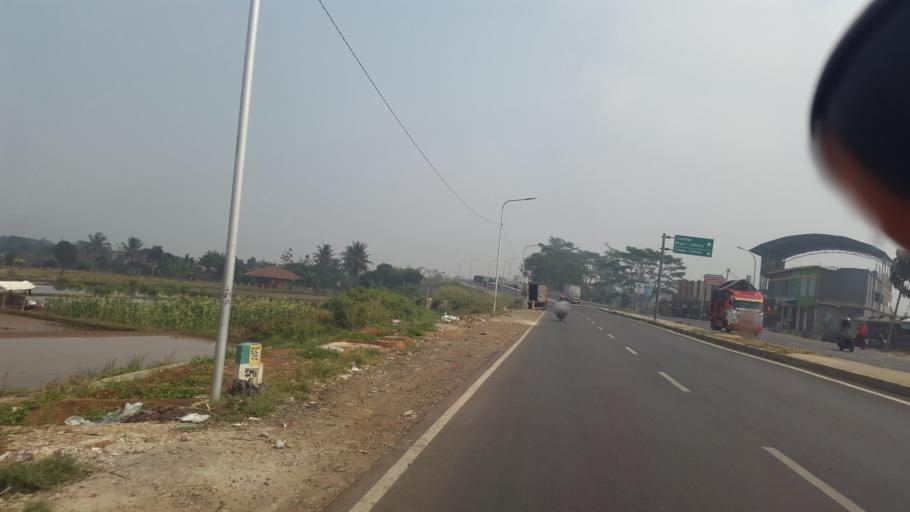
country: ID
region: West Java
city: Sukabumi
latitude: -6.9134
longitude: 106.8798
